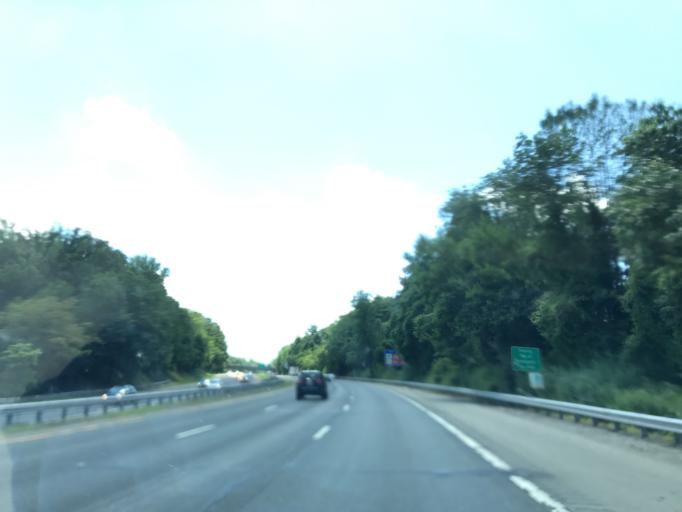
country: US
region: New Jersey
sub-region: Morris County
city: Boonton
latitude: 40.8972
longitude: -74.4155
